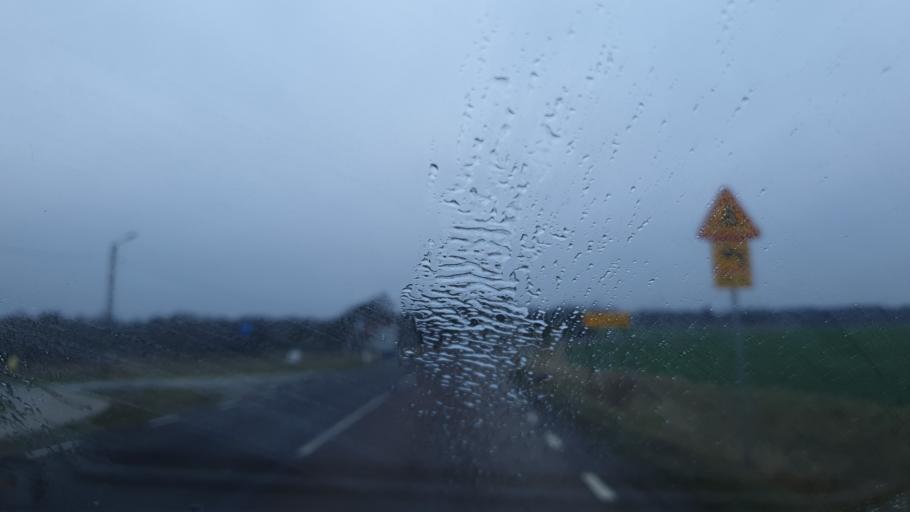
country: SE
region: Blekinge
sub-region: Karlskrona Kommun
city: Sturko
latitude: 56.1750
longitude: 15.7225
